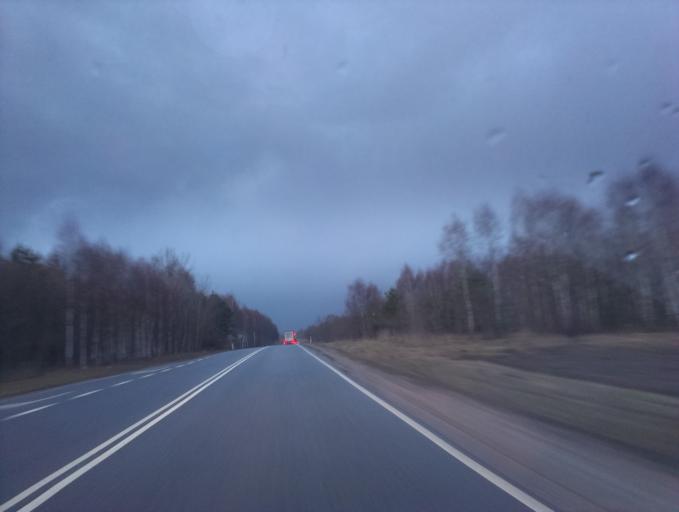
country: PL
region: Lodz Voivodeship
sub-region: Powiat opoczynski
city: Zarnow
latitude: 51.2307
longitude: 20.1777
